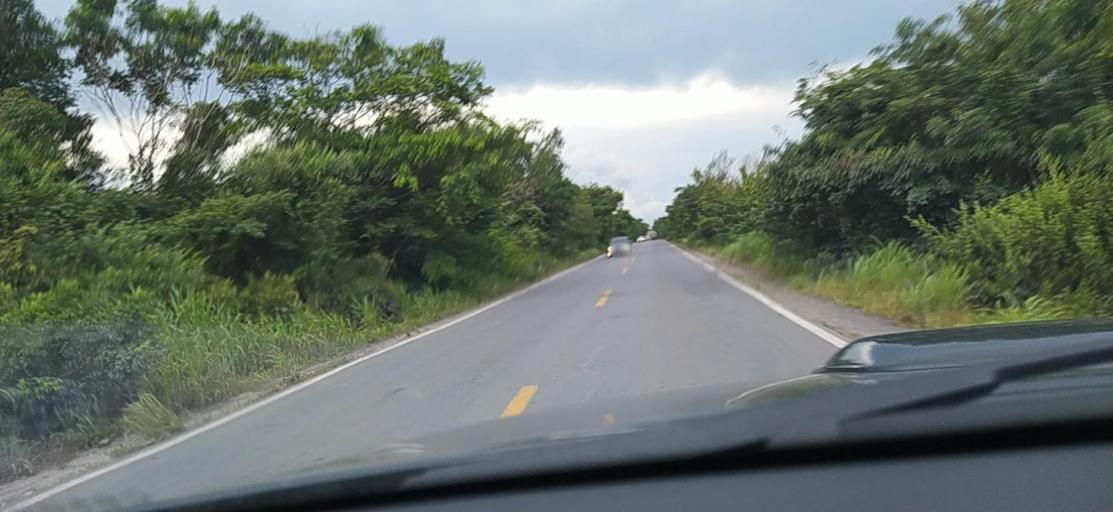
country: BR
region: Minas Gerais
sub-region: Francisco Sa
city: Francisco Sa
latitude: -16.2348
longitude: -43.6174
